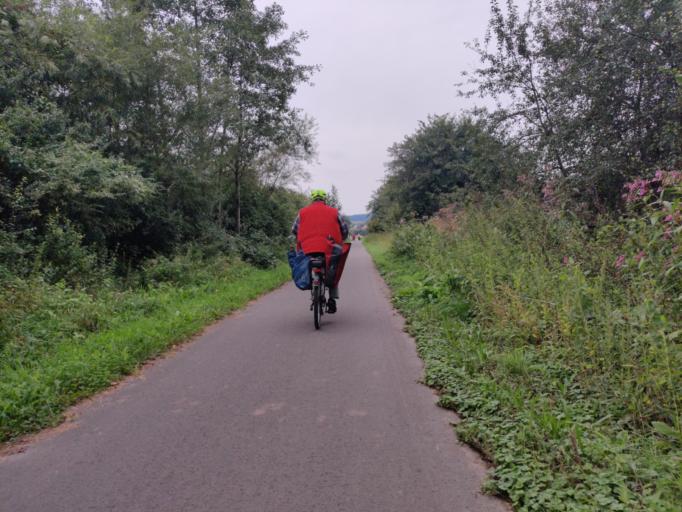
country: DE
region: Lower Saxony
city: Heinsen
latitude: 51.9029
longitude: 9.4492
